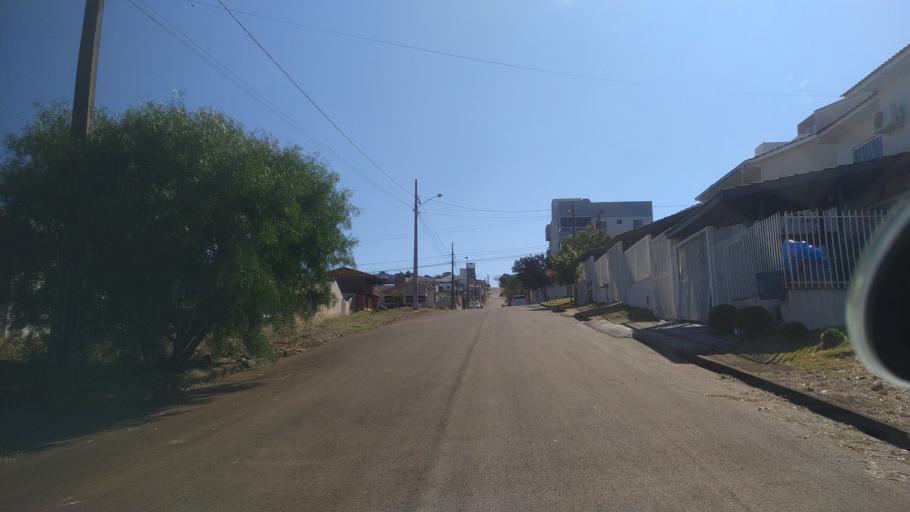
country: BR
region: Santa Catarina
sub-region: Chapeco
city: Chapeco
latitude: -27.0930
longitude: -52.5858
